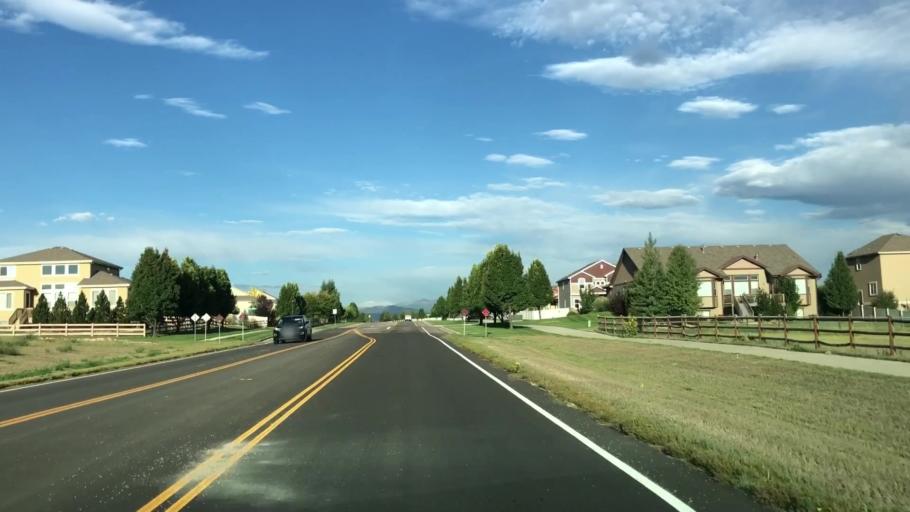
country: US
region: Colorado
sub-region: Weld County
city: Windsor
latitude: 40.4422
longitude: -104.9628
